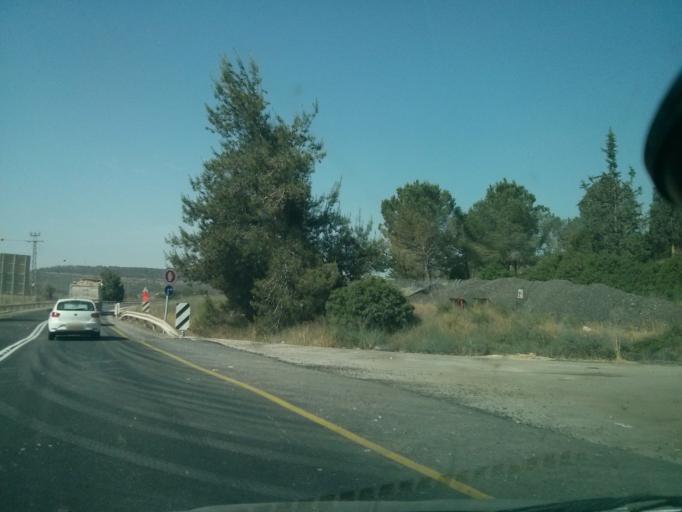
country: IL
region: Jerusalem
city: Bet Shemesh
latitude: 31.6944
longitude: 35.0104
